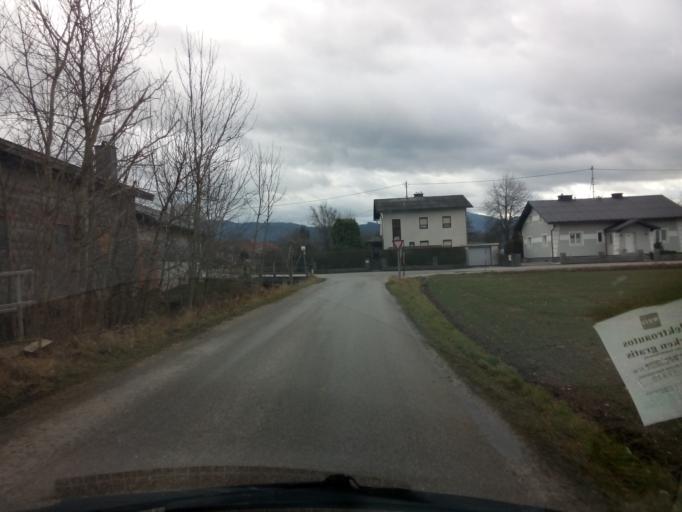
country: AT
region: Upper Austria
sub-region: Politischer Bezirk Gmunden
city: Scharnstein
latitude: 47.9768
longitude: 14.0183
